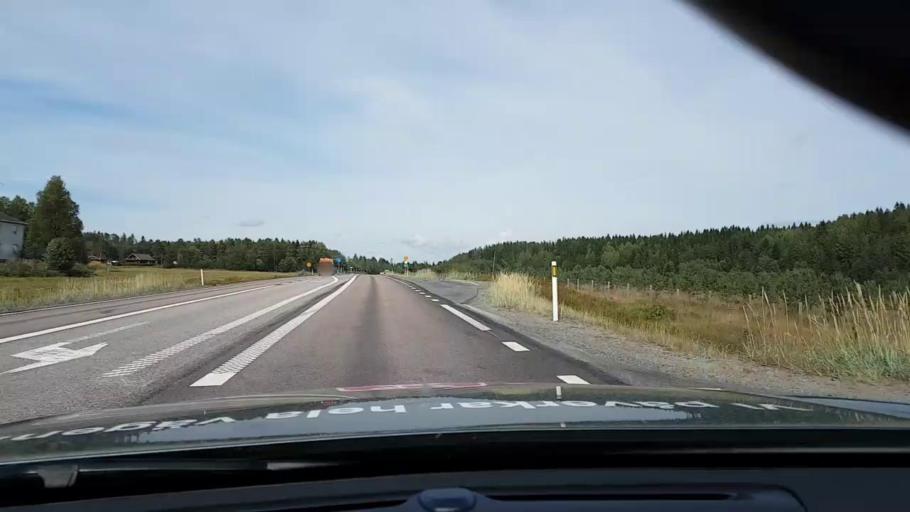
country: SE
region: Vaesternorrland
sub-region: OErnskoeldsviks Kommun
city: Husum
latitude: 63.4154
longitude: 19.2059
